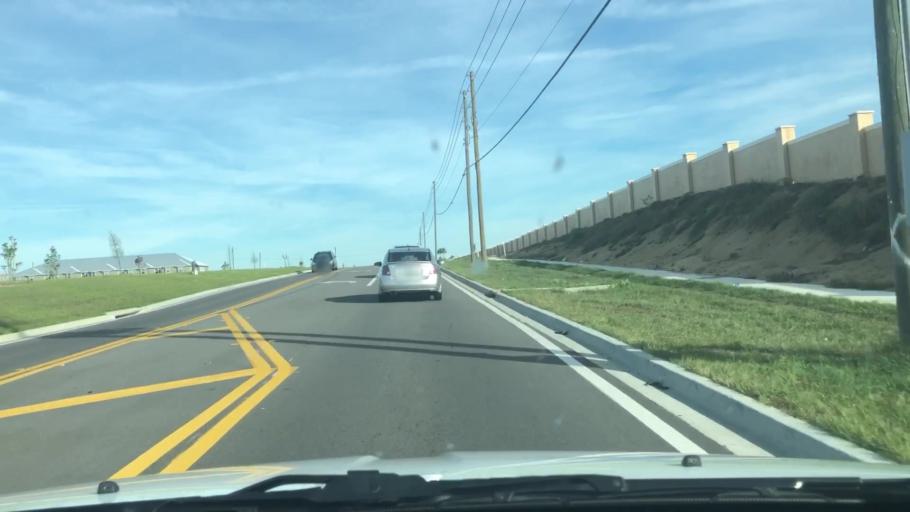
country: US
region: Florida
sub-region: Polk County
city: Davenport
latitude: 28.1576
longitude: -81.6282
